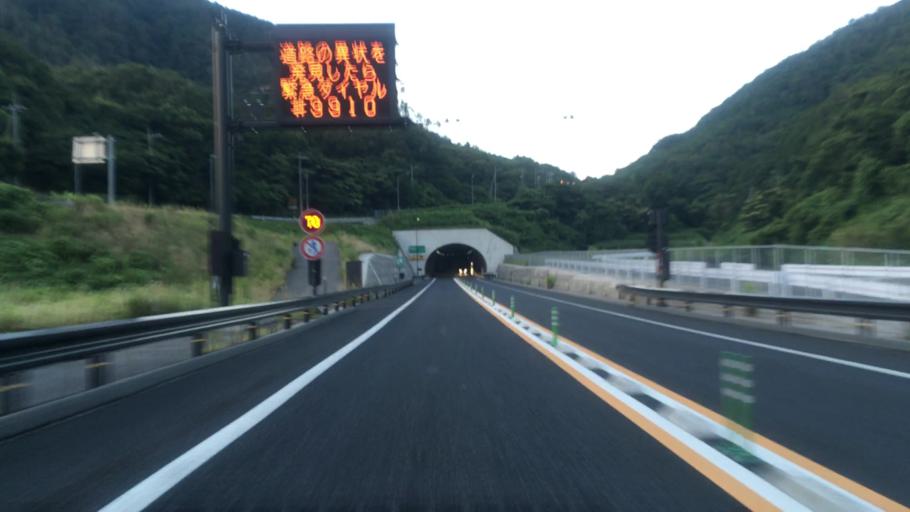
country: JP
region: Tottori
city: Tottori
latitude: 35.5598
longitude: 134.2840
